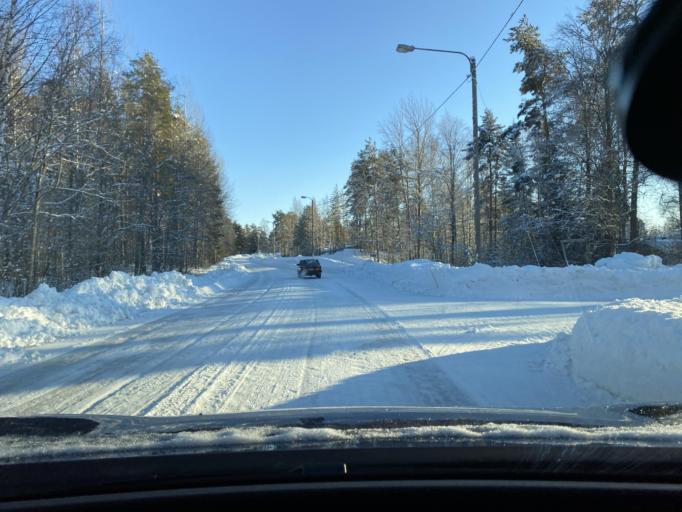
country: FI
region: Southern Savonia
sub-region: Mikkeli
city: Kangasniemi
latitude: 61.9950
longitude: 26.6313
